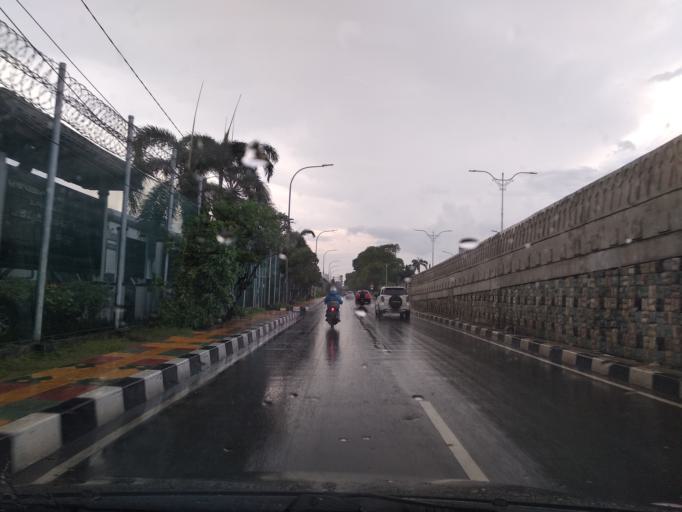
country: ID
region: Jakarta Raya
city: Jakarta
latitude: -6.2145
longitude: 106.8859
